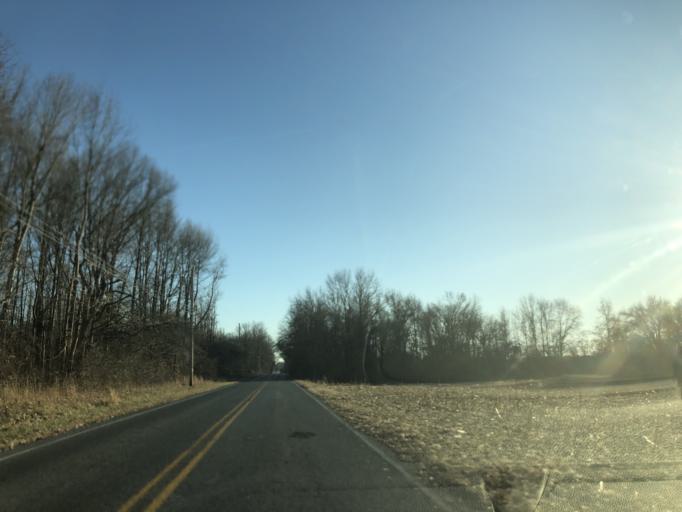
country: US
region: New Jersey
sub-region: Gloucester County
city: Beckett
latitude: 39.7290
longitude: -75.4058
